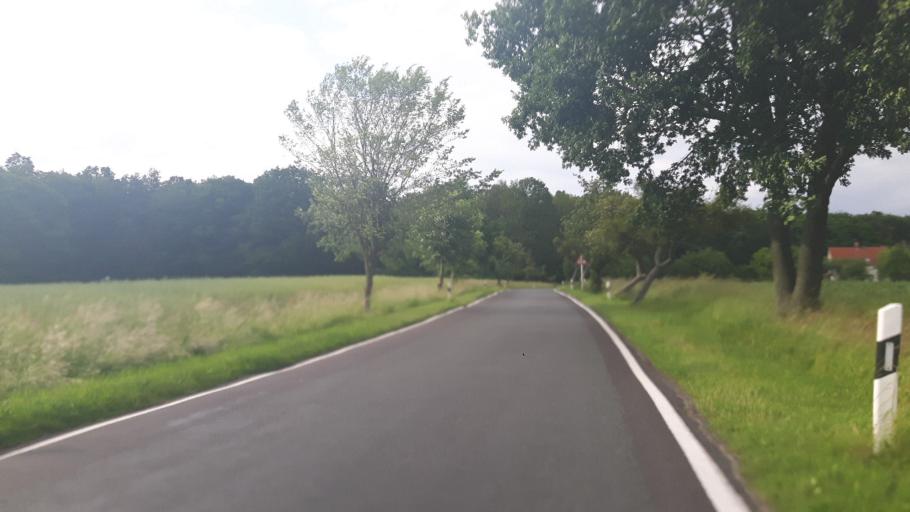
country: DE
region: Brandenburg
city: Hohenfinow
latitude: 52.7778
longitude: 13.8933
